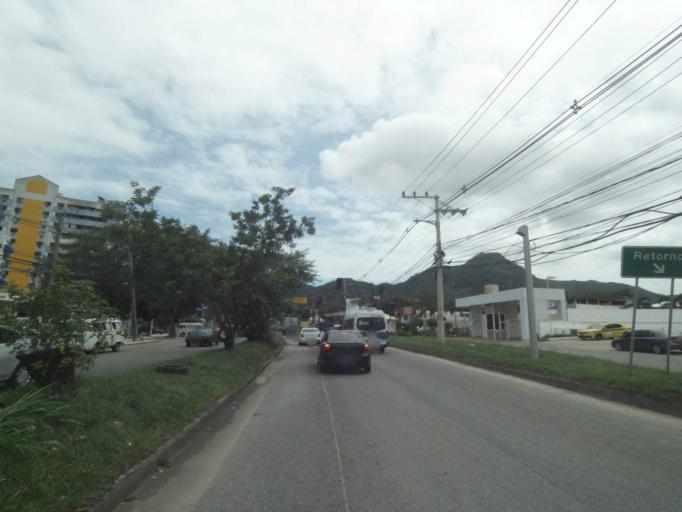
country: BR
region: Rio de Janeiro
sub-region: Nilopolis
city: Nilopolis
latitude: -22.9672
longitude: -43.4127
